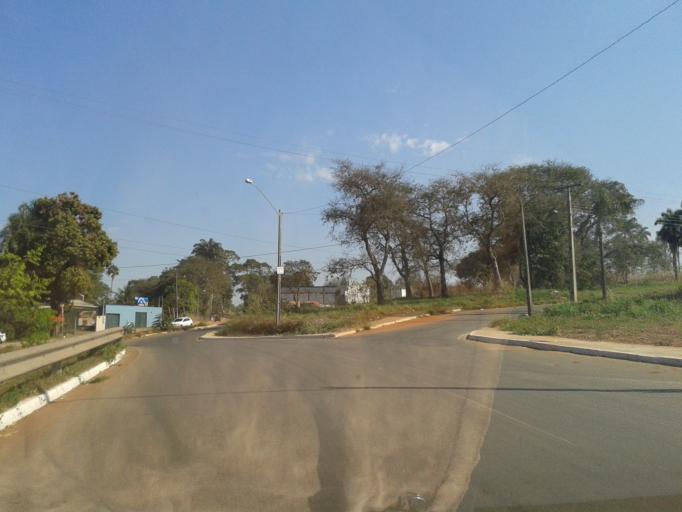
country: BR
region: Goias
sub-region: Aparecida De Goiania
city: Aparecida de Goiania
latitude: -16.7659
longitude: -49.3026
